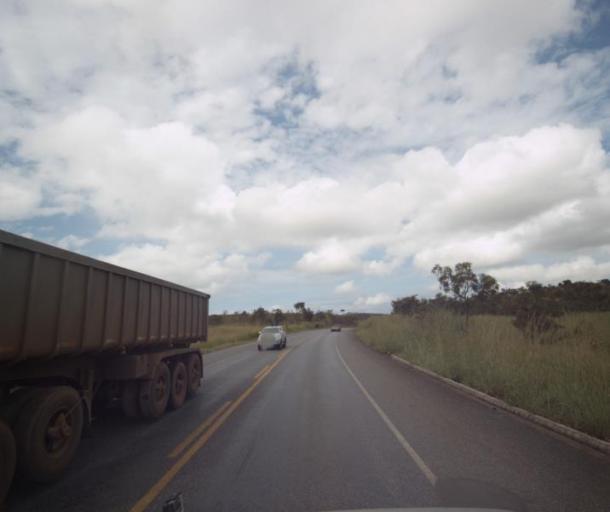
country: BR
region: Goias
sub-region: Pirenopolis
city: Pirenopolis
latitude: -15.6037
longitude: -48.6449
